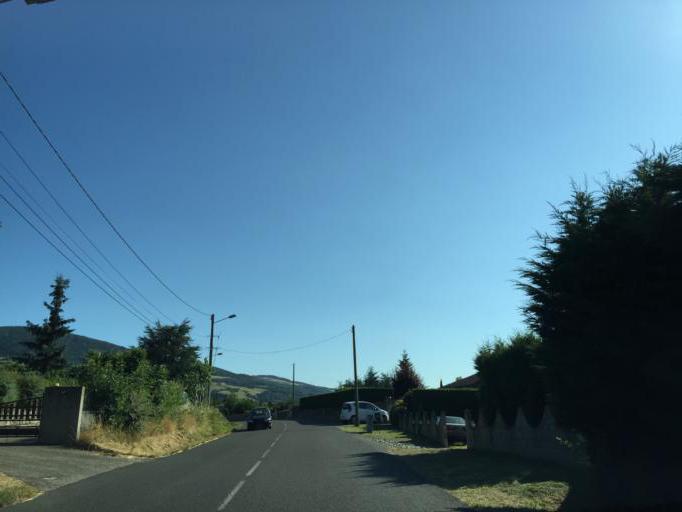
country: FR
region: Rhone-Alpes
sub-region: Departement de la Loire
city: Saint-Jean-Bonnefonds
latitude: 45.4559
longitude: 4.4878
